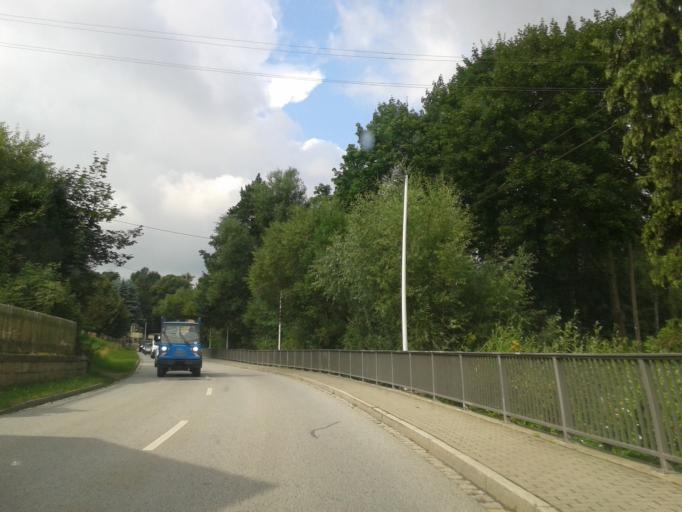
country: DE
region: Saxony
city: Durrrohrsdorf
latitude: 51.0363
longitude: 13.9479
